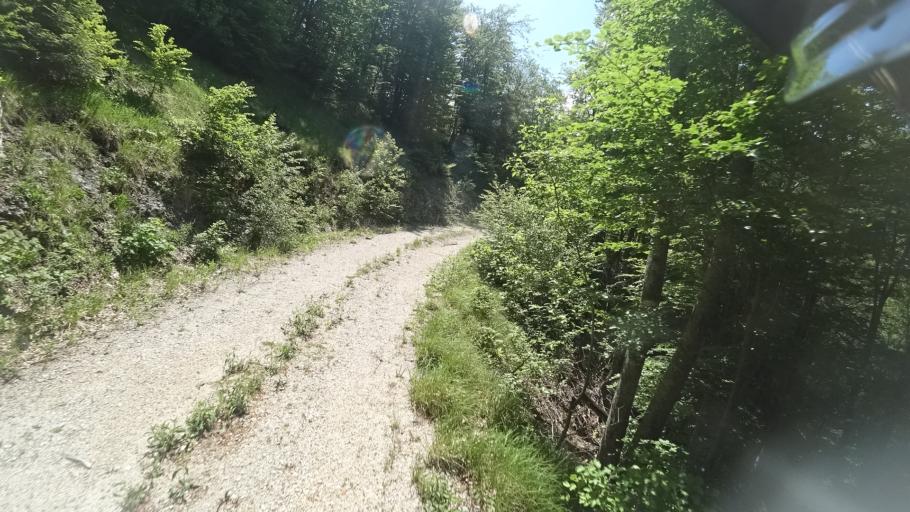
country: BA
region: Federation of Bosnia and Herzegovina
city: Orasac
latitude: 44.5652
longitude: 15.8532
